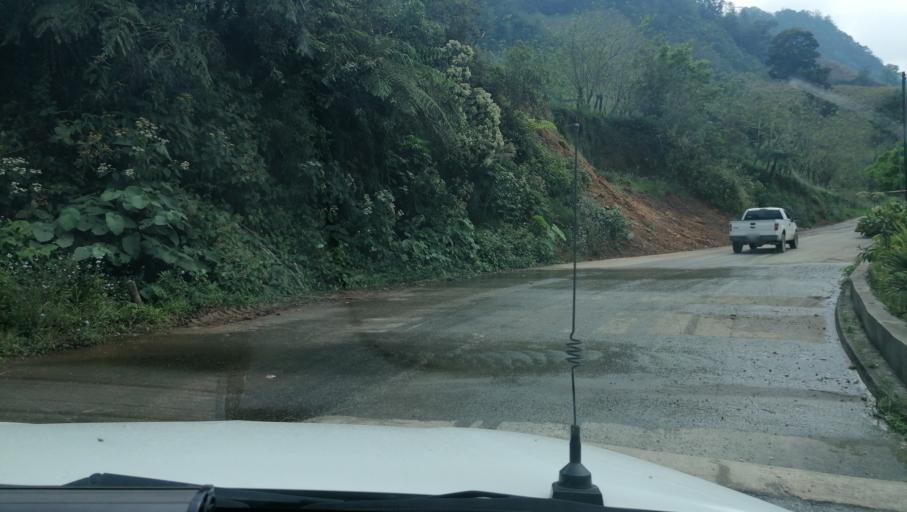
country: MX
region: Chiapas
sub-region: Francisco Leon
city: San Miguel la Sardina
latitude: 17.2496
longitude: -93.2824
